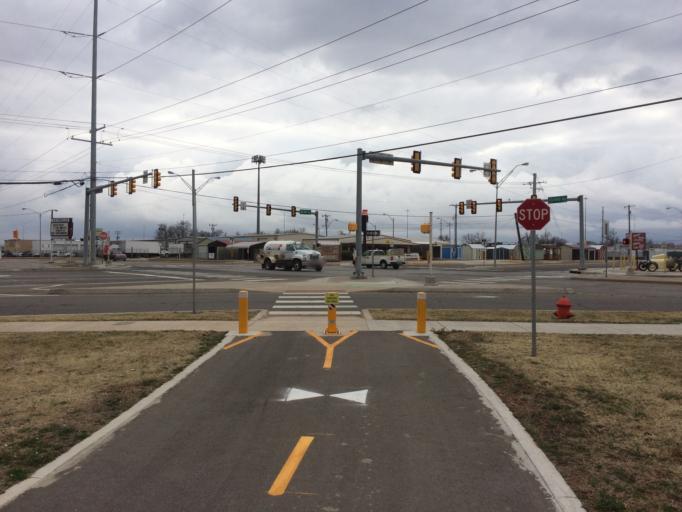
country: US
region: Oklahoma
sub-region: Oklahoma County
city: Oklahoma City
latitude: 35.4645
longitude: -97.5660
